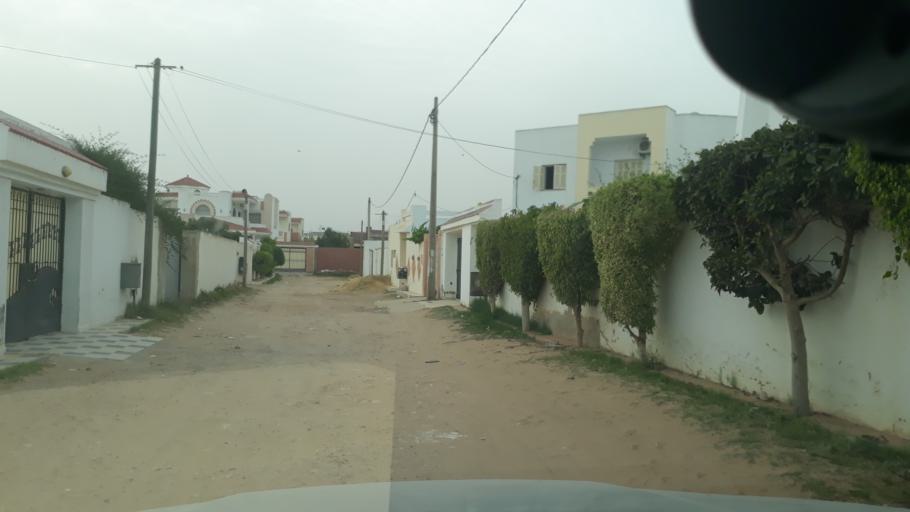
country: TN
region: Safaqis
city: Al Qarmadah
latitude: 34.7834
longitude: 10.7701
